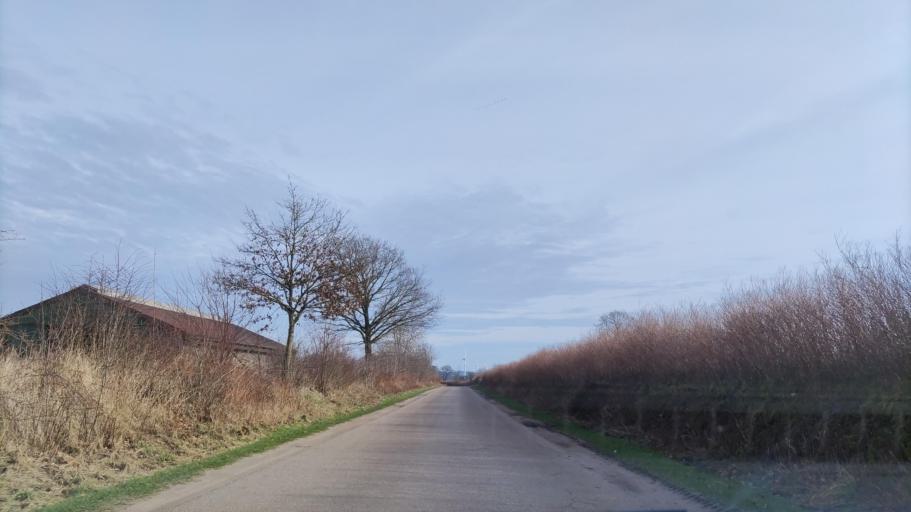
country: DE
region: Schleswig-Holstein
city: Kropp
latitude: 54.4126
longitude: 9.5334
